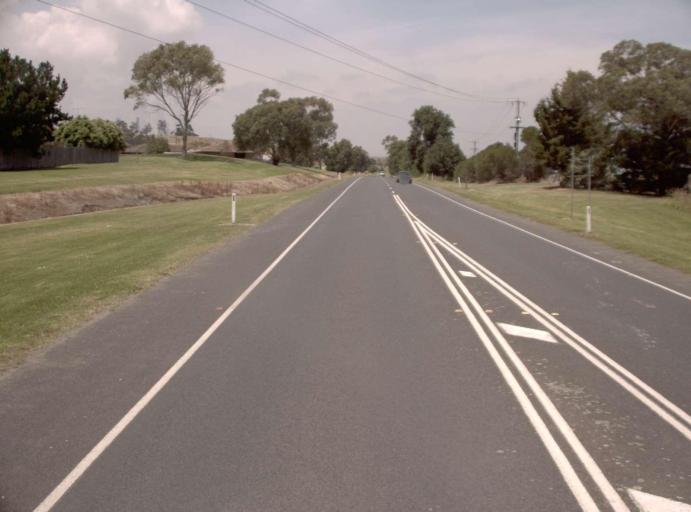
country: AU
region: Victoria
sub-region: Latrobe
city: Traralgon
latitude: -38.2100
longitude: 146.5451
